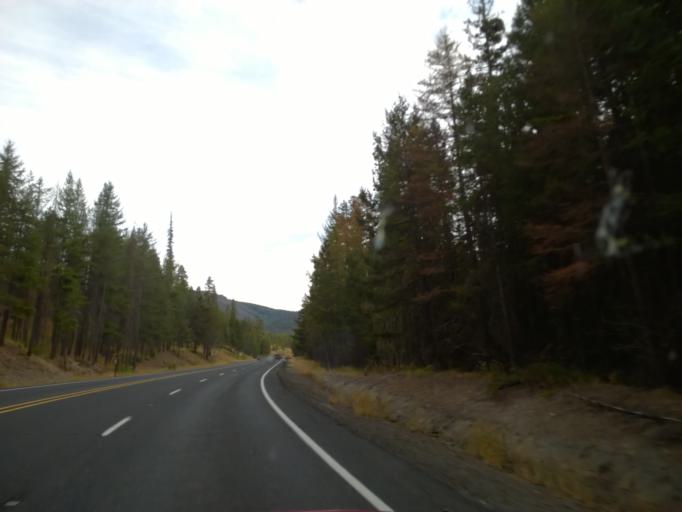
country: US
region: Washington
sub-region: Chelan County
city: Cashmere
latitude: 47.3449
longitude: -120.5660
